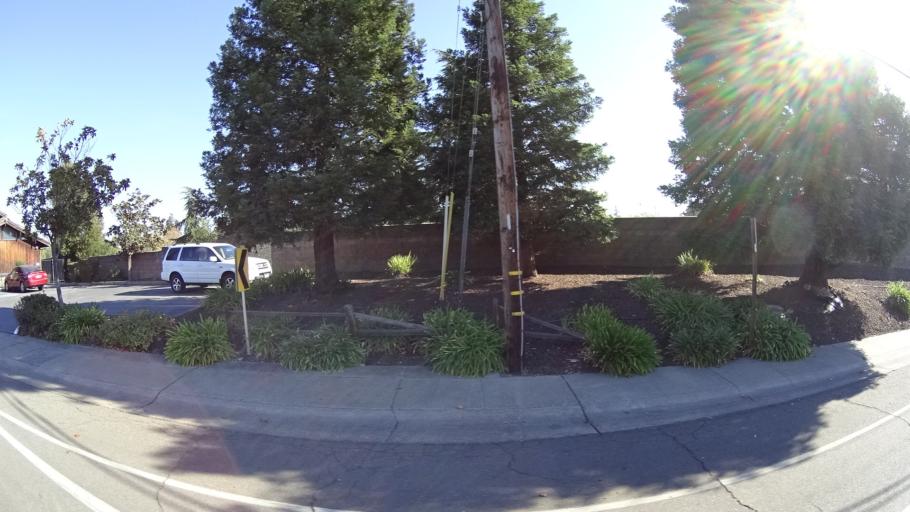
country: US
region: California
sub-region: Sacramento County
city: Antelope
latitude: 38.7028
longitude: -121.3157
